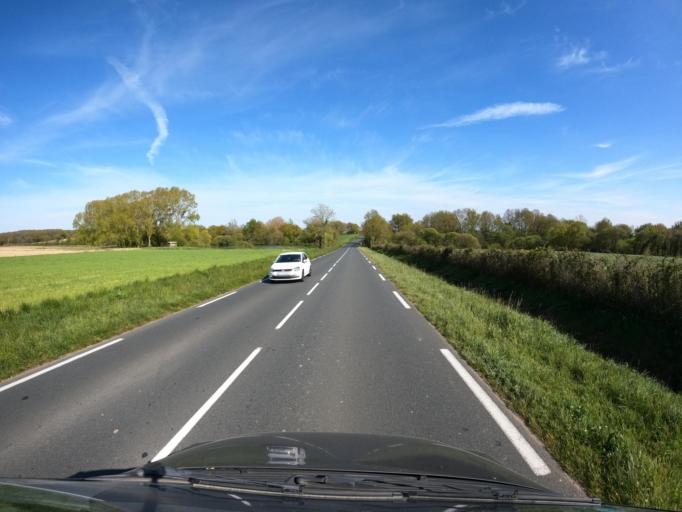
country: FR
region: Pays de la Loire
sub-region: Departement de Maine-et-Loire
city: La Seguiniere
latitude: 47.0740
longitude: -0.9287
